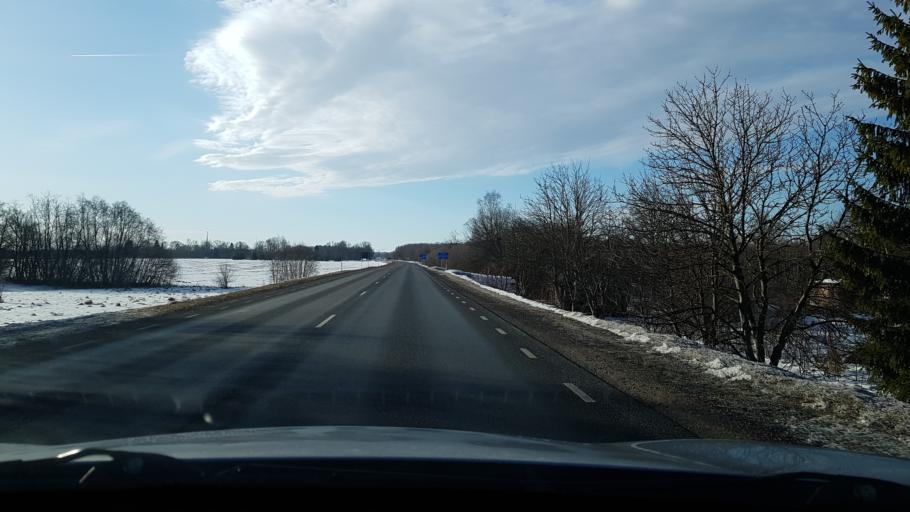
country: EE
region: Viljandimaa
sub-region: Vohma linn
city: Vohma
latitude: 58.6375
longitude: 25.5750
